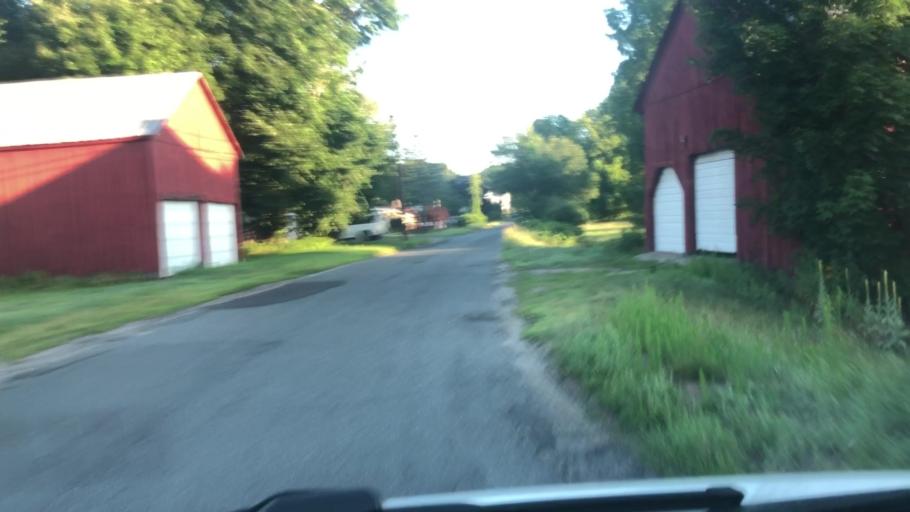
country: US
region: Massachusetts
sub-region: Hampshire County
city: Southampton
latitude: 42.2458
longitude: -72.7112
